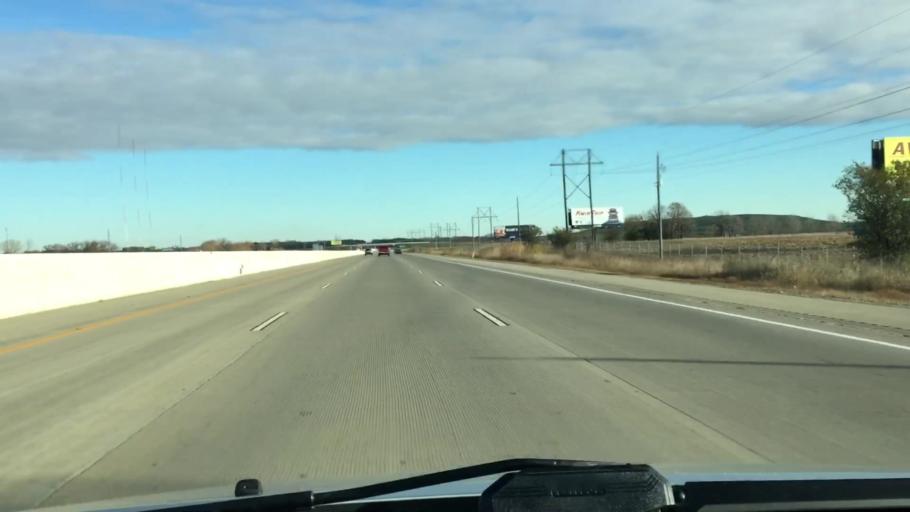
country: US
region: Wisconsin
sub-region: Winnebago County
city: Oshkosh
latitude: 44.0731
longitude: -88.5660
